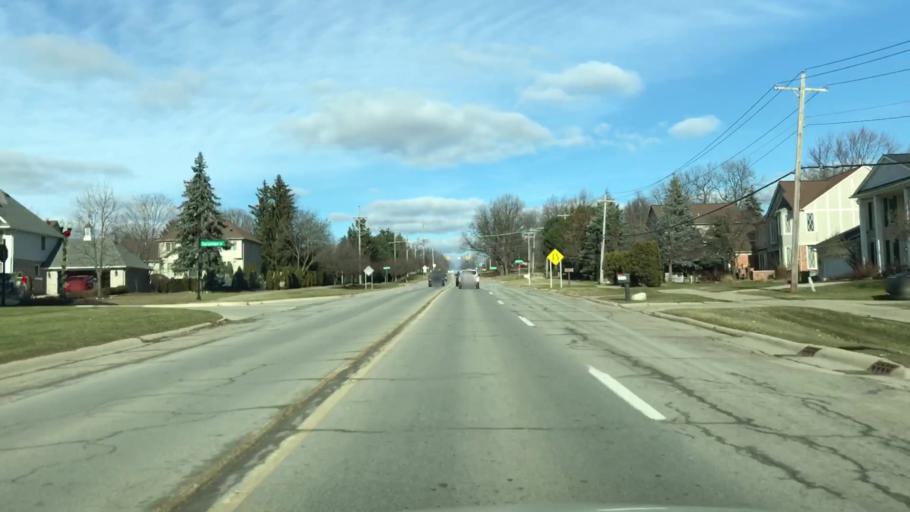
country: US
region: Michigan
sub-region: Oakland County
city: Auburn Hills
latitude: 42.7070
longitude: -83.1952
